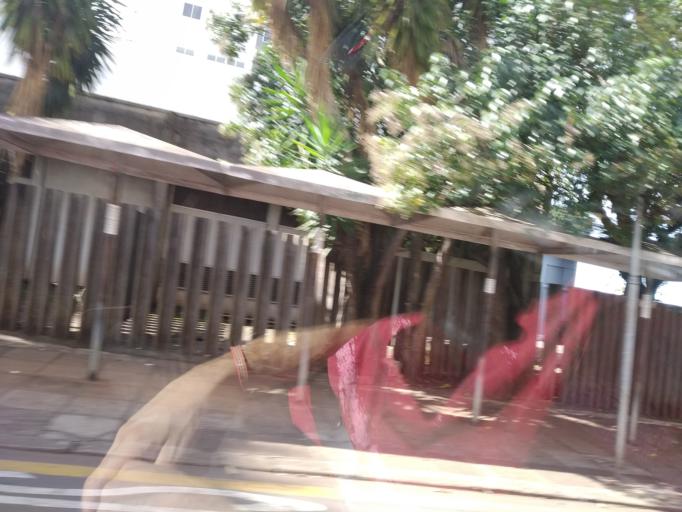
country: BR
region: Parana
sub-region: Pato Branco
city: Pato Branco
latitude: -26.2284
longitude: -52.6742
